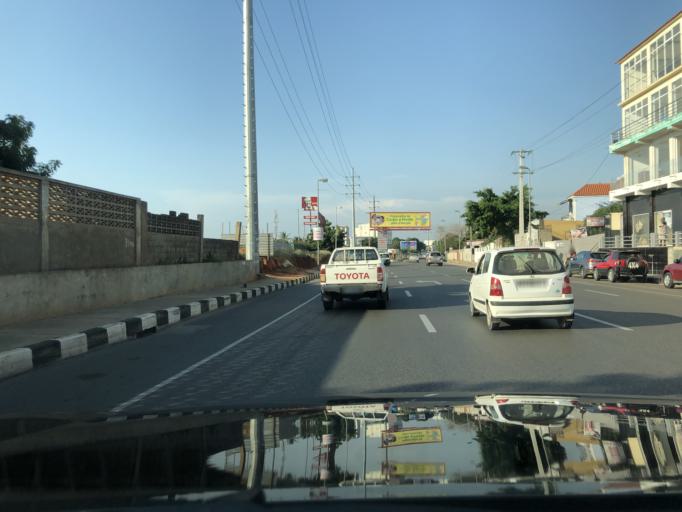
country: AO
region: Luanda
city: Luanda
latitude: -8.8957
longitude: 13.1807
